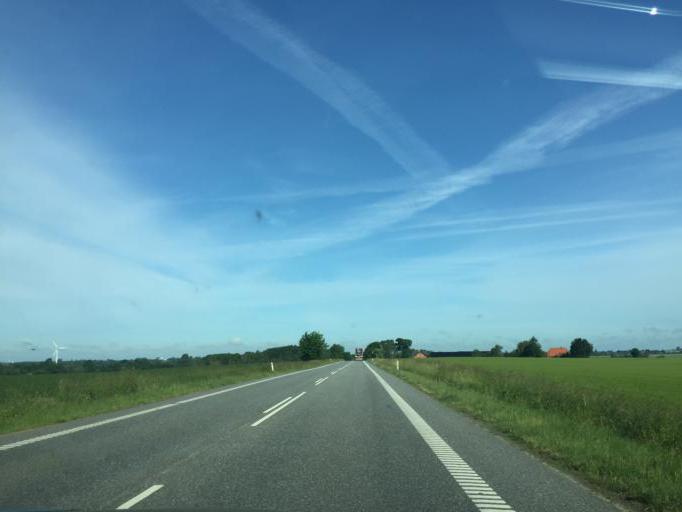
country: DK
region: South Denmark
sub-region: Middelfart Kommune
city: Ejby
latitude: 55.4603
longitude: 9.9348
